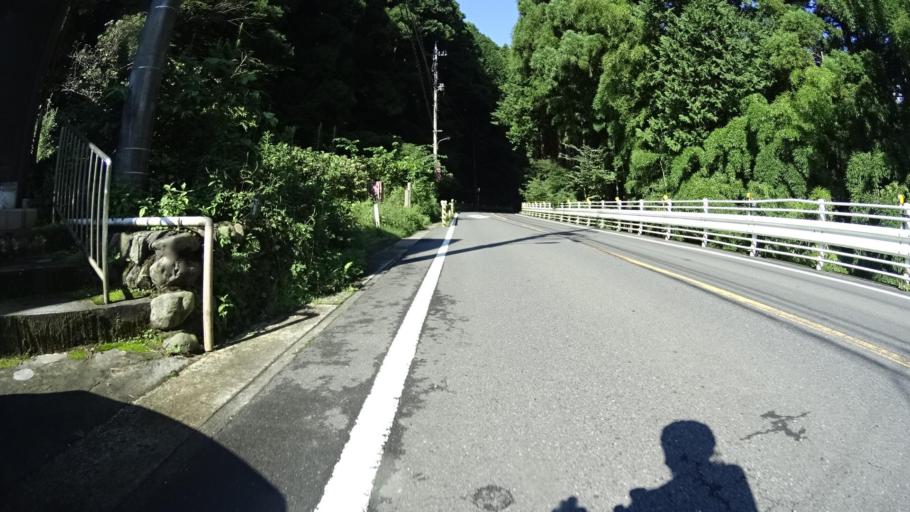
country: JP
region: Tokyo
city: Itsukaichi
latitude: 35.7287
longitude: 139.1457
